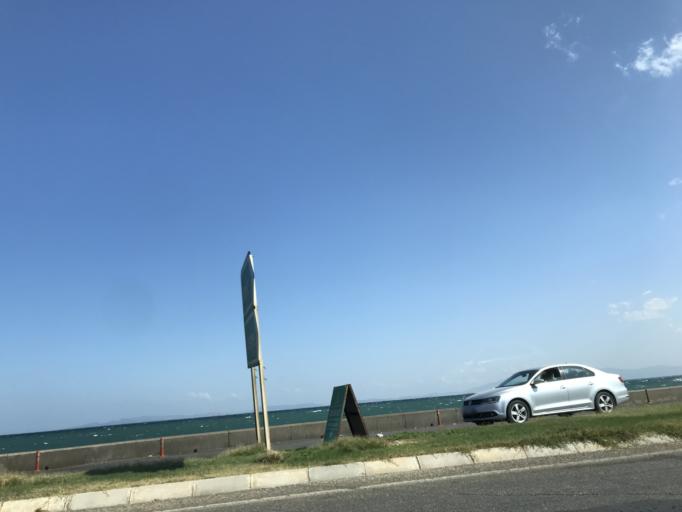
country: TR
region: Izmir
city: Urla
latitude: 38.3753
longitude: 26.8746
